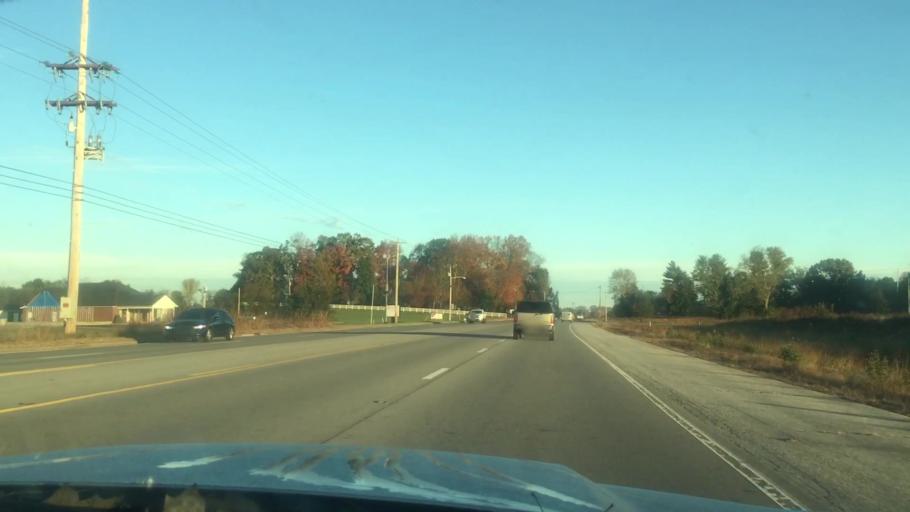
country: US
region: Tennessee
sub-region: Franklin County
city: Estill Springs
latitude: 35.2466
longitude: -86.1182
